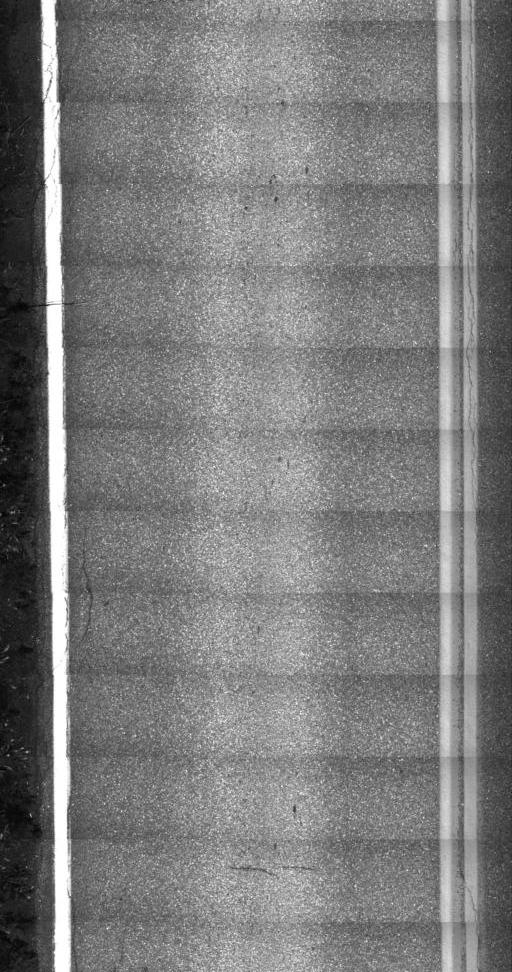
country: US
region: Vermont
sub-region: Windham County
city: Dover
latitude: 42.7991
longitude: -72.8231
